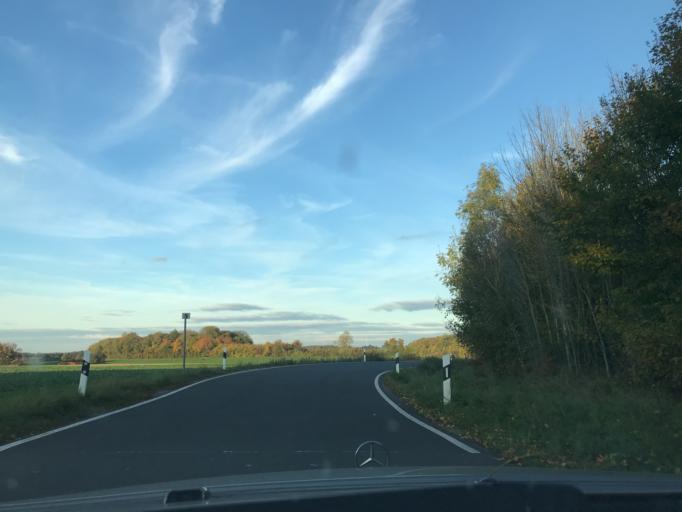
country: DE
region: Lower Saxony
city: Juhnde
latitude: 51.4096
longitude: 9.8229
